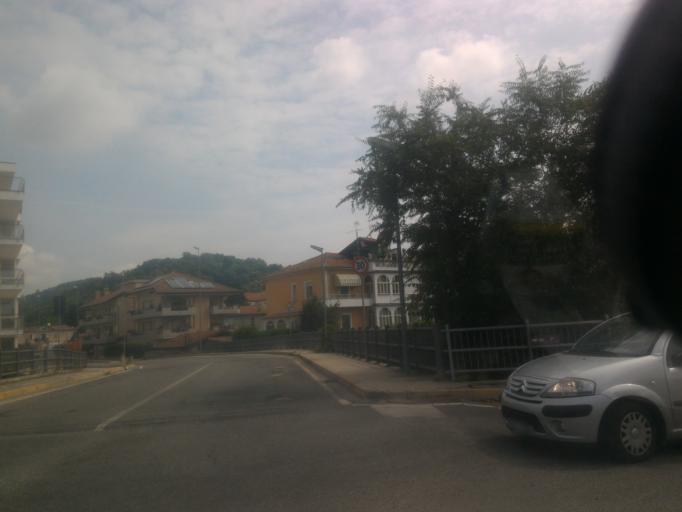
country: IT
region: Piedmont
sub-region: Provincia di Torino
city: Pinerolo
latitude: 44.8843
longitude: 7.3183
